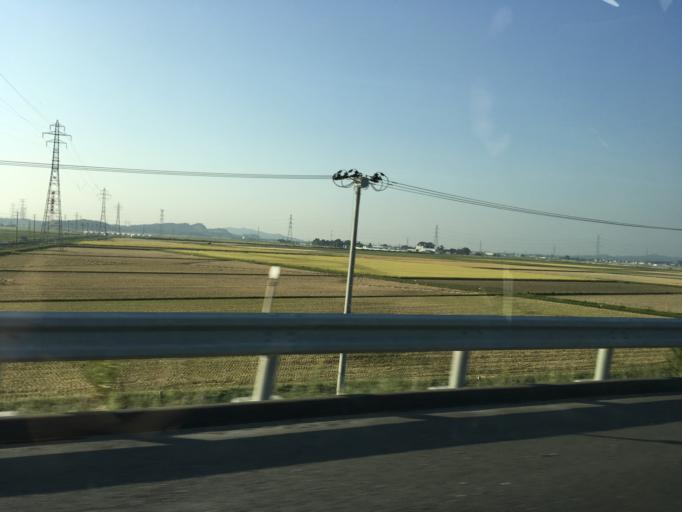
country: JP
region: Miyagi
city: Ishinomaki
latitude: 38.4570
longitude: 141.2756
